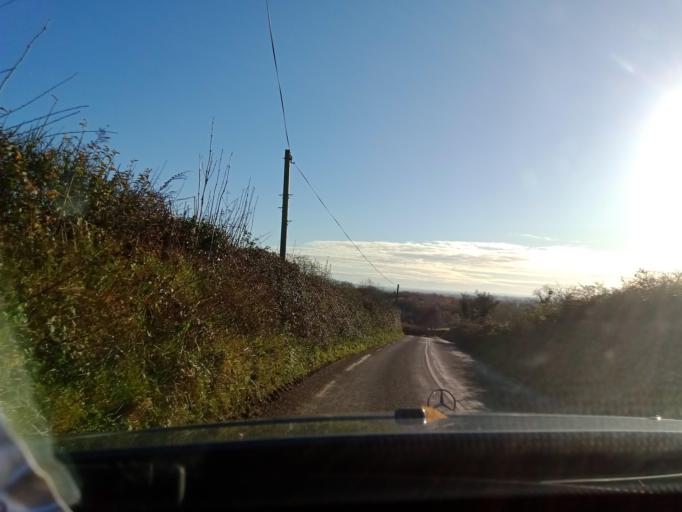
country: IE
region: Leinster
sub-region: Kilkenny
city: Piltown
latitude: 52.3939
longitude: -7.3512
